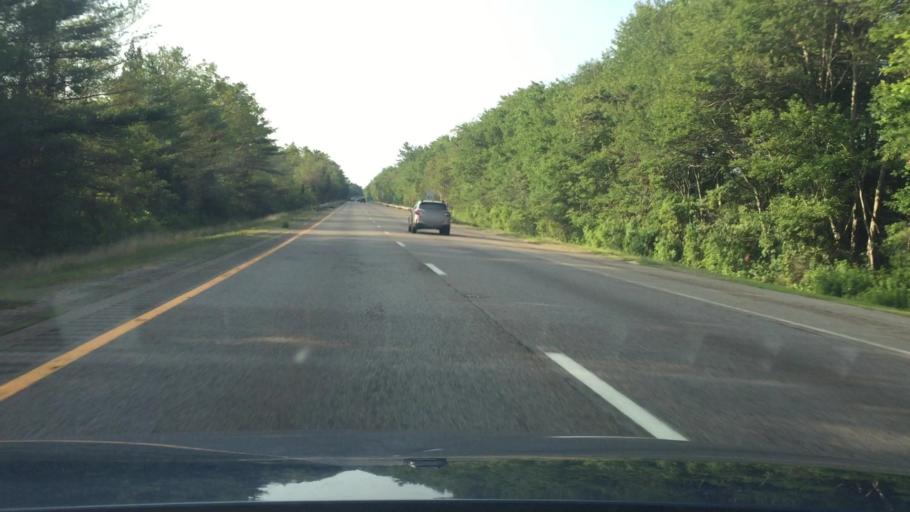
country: US
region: Massachusetts
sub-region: Plymouth County
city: Marshfield
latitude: 42.0770
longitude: -70.7367
